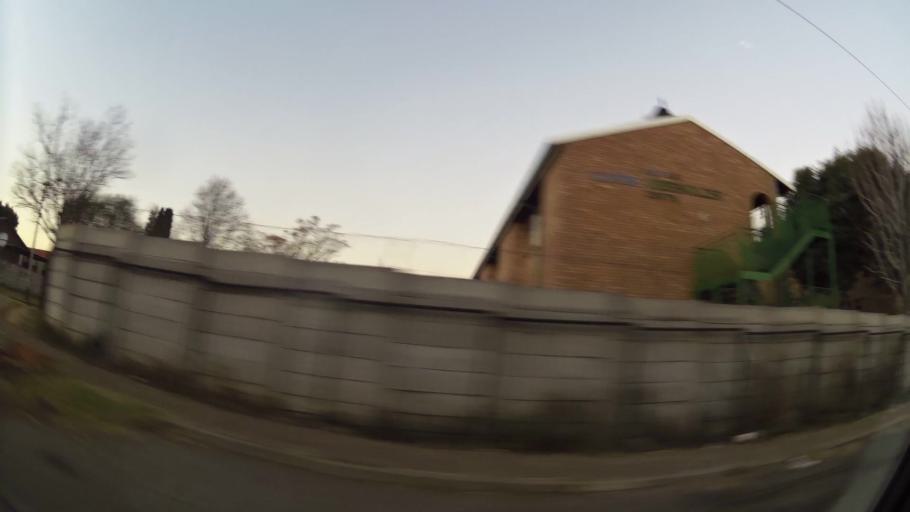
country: ZA
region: Gauteng
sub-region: Ekurhuleni Metropolitan Municipality
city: Germiston
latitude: -26.2628
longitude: 28.1630
